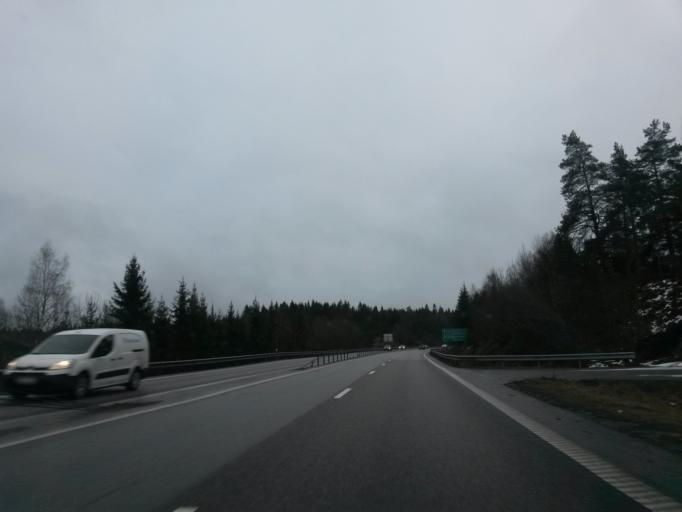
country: SE
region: Vaestra Goetaland
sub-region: Uddevalla Kommun
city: Uddevalla
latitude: 58.3446
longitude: 11.9882
